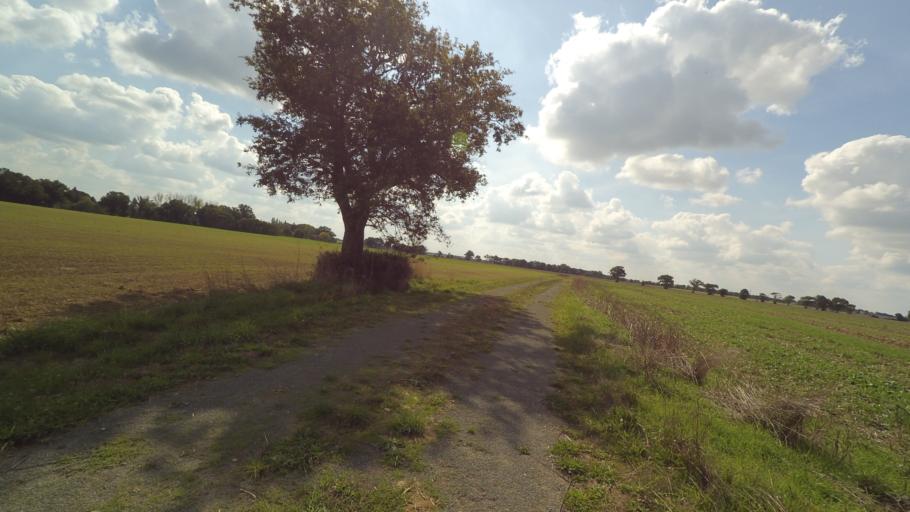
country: FR
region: Pays de la Loire
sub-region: Departement de la Vendee
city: Bouffere
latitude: 46.9675
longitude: -1.3737
